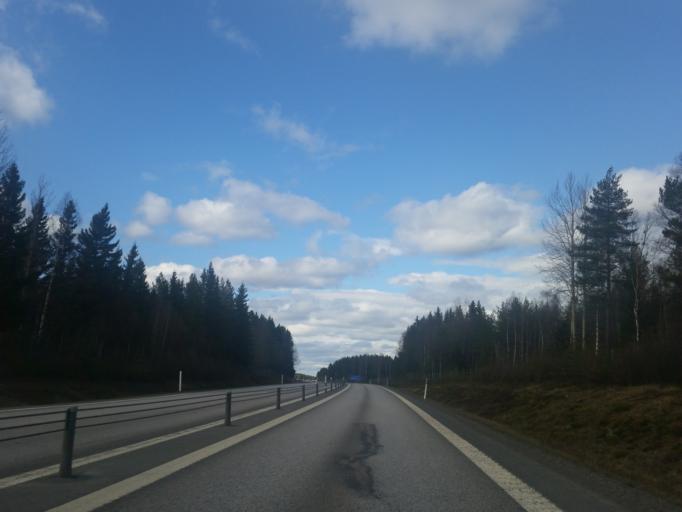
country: SE
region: Vaesterbotten
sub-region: Robertsfors Kommun
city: Robertsfors
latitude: 64.0838
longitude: 20.8680
